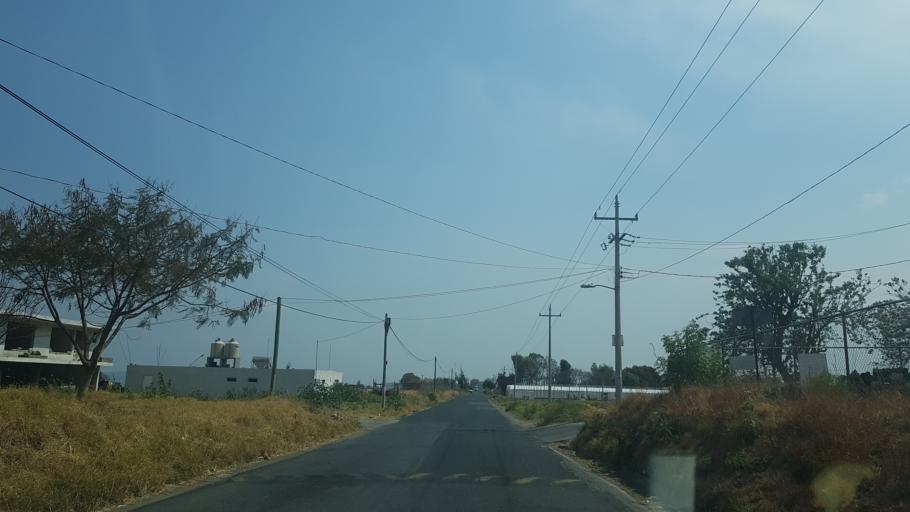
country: MX
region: Puebla
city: San Juan Tianguismanalco
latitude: 18.9422
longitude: -98.4540
